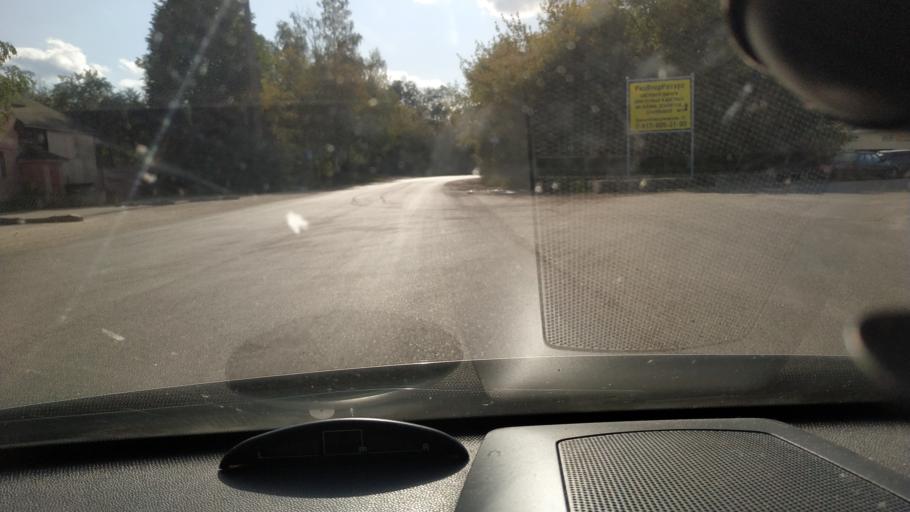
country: RU
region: Rjazan
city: Ryazan'
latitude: 54.6694
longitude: 39.6200
